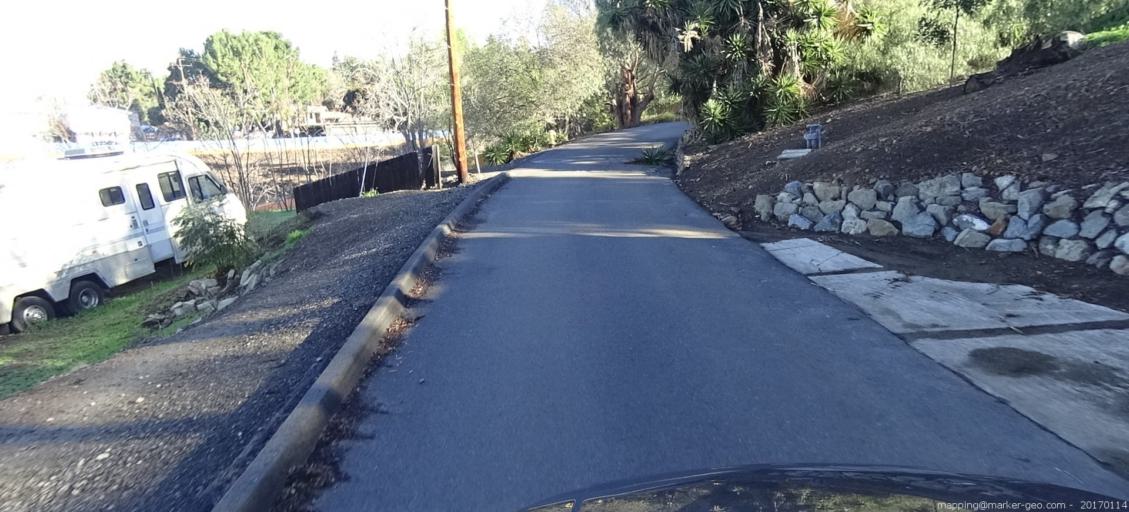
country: US
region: California
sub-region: Orange County
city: North Tustin
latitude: 33.7847
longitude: -117.8027
